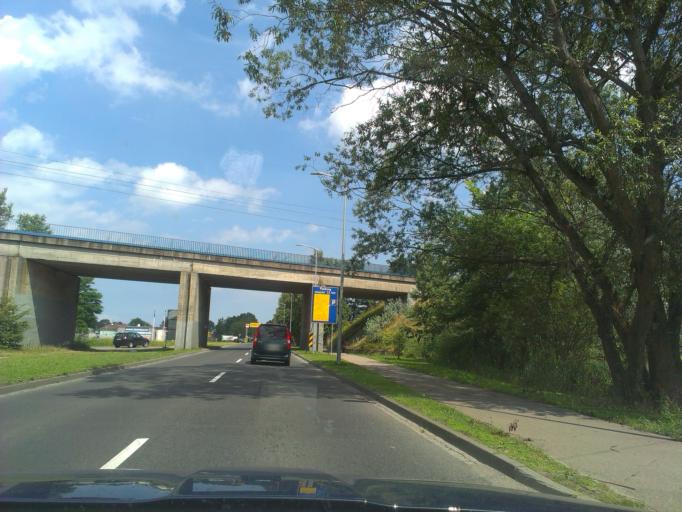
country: PL
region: West Pomeranian Voivodeship
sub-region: Powiat kamienski
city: Miedzyzdroje
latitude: 53.9146
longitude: 14.4352
